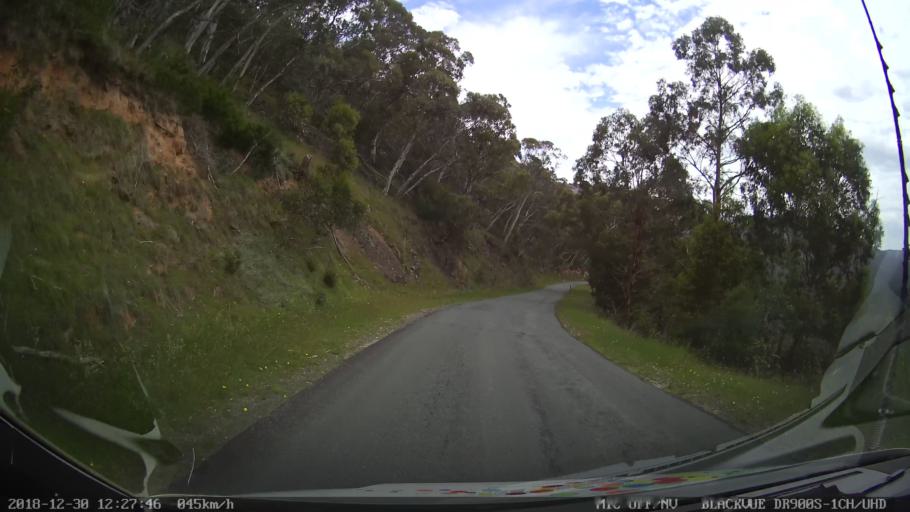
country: AU
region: New South Wales
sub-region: Snowy River
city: Jindabyne
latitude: -36.3288
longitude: 148.4894
